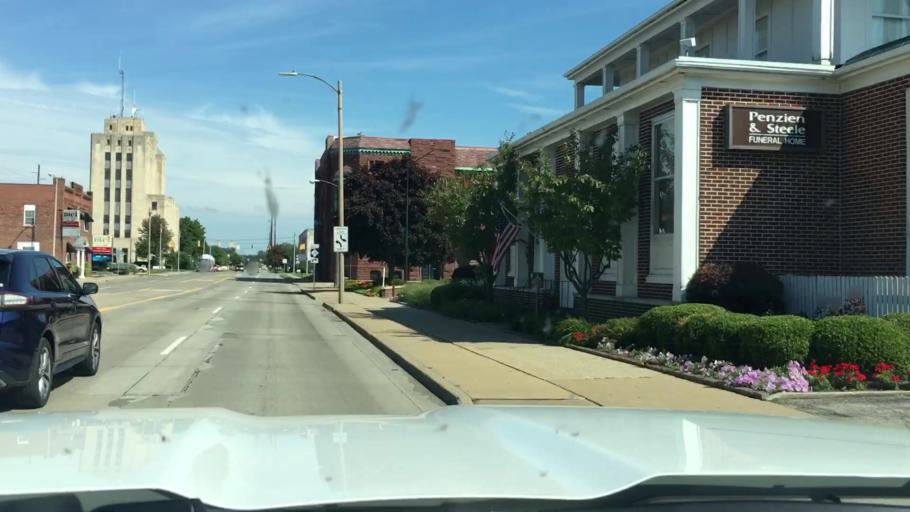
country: US
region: Michigan
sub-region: Bay County
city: Bay City
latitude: 43.5960
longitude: -83.8847
